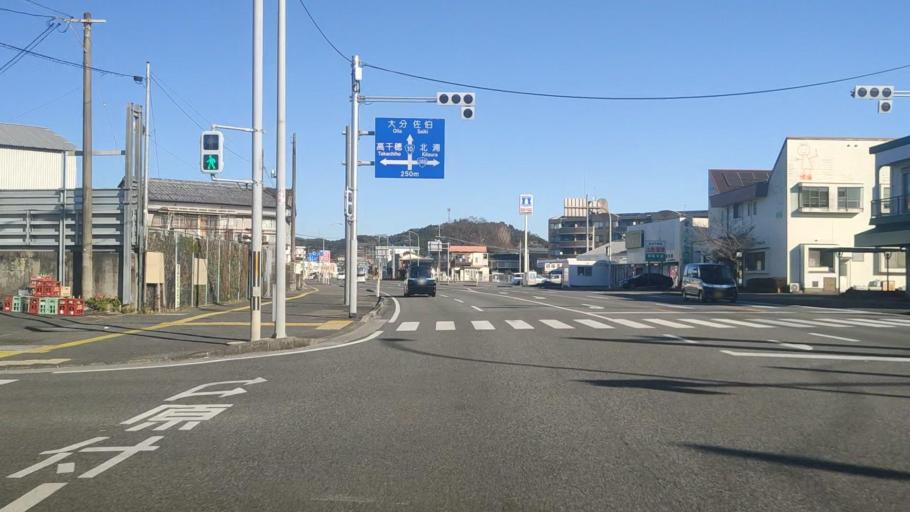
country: JP
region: Miyazaki
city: Nobeoka
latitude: 32.6011
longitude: 131.6825
